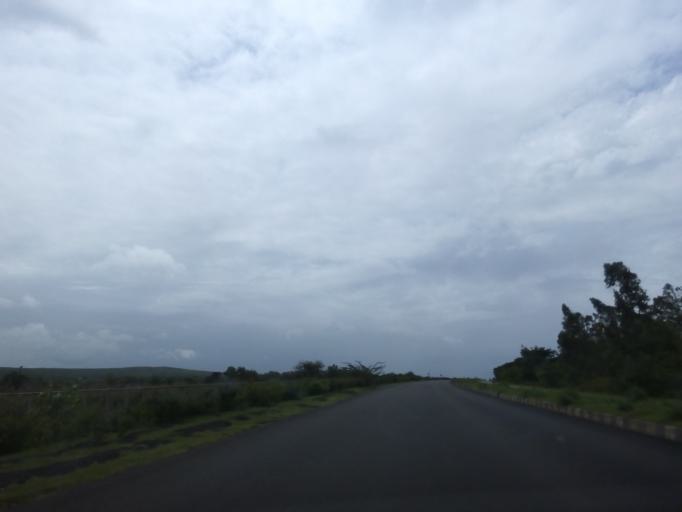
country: IN
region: Karnataka
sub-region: Haveri
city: Byadgi
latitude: 14.7098
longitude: 75.5101
